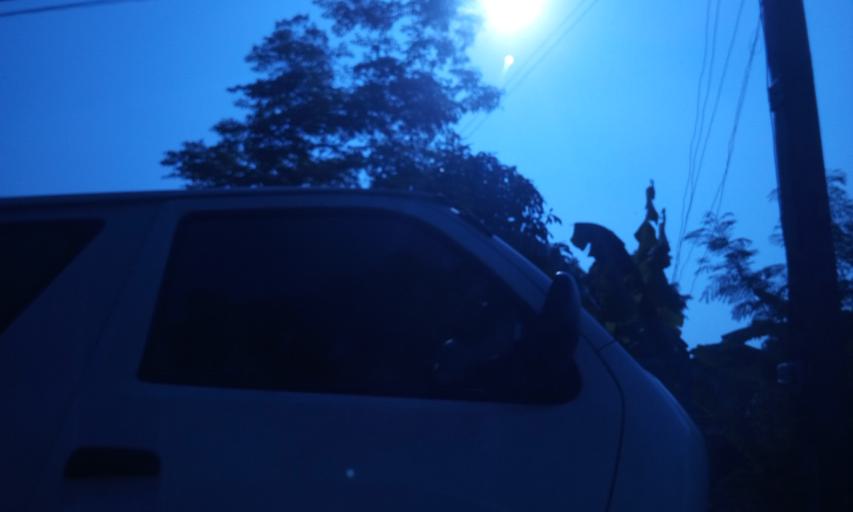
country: TH
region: Pathum Thani
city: Lam Luk Ka
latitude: 13.9594
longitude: 100.7058
